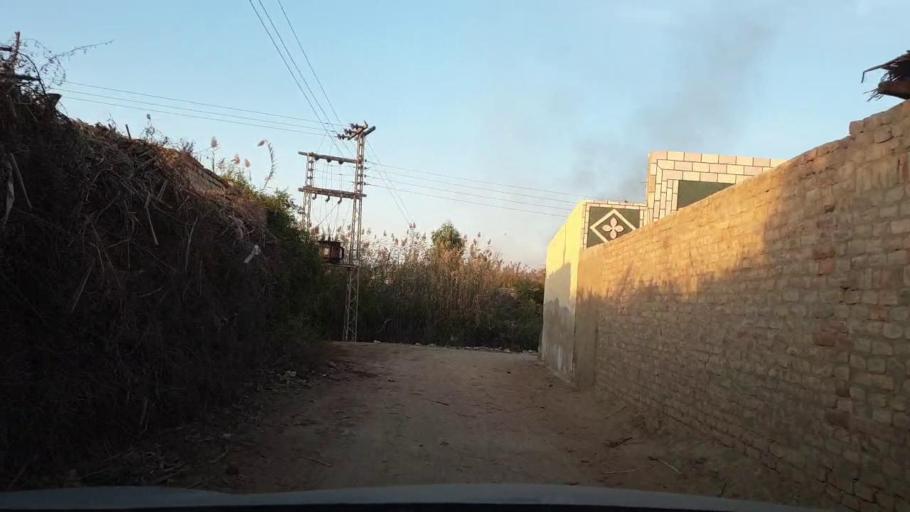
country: PK
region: Sindh
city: Tando Allahyar
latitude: 25.6094
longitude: 68.6857
